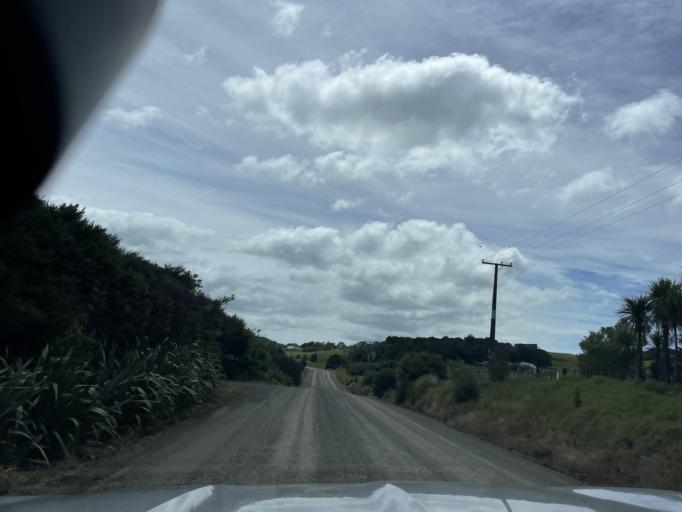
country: NZ
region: Auckland
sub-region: Auckland
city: Wellsford
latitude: -36.1673
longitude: 174.2809
